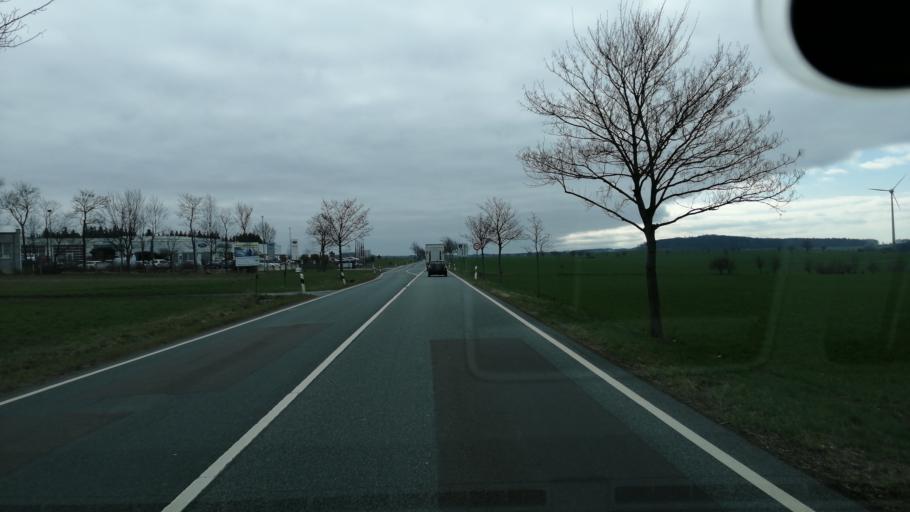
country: DE
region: Saxony
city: Lobau
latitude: 51.0768
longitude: 14.6779
